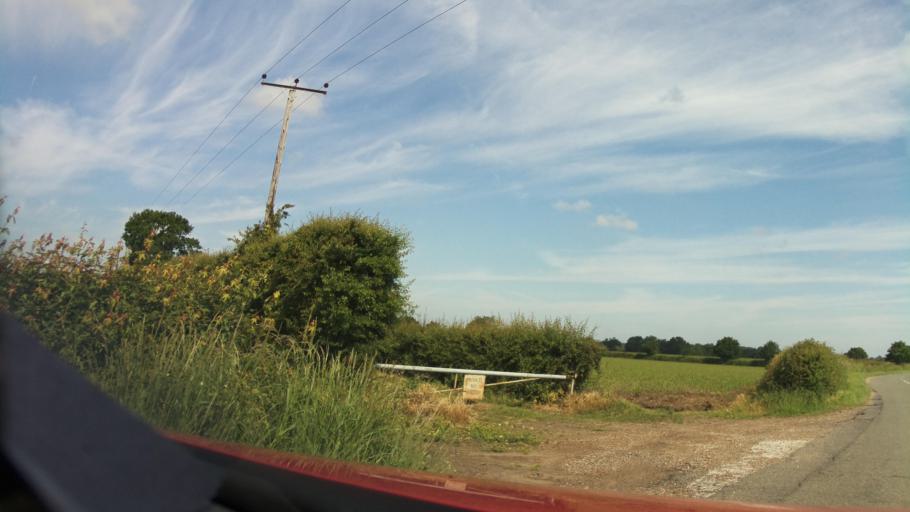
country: GB
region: England
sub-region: Lincolnshire
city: Skellingthorpe
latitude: 53.1395
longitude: -0.6332
